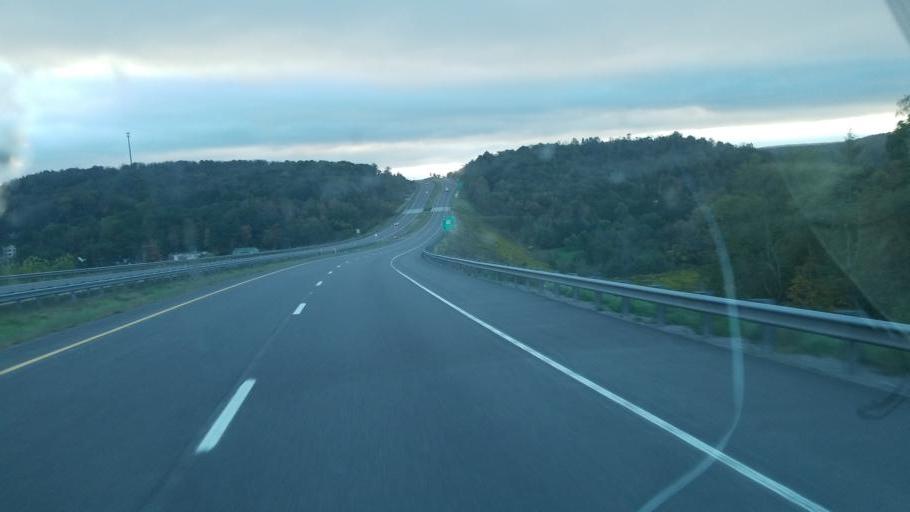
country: US
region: Pennsylvania
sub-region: Somerset County
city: Meyersdale
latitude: 39.6945
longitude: -79.1766
